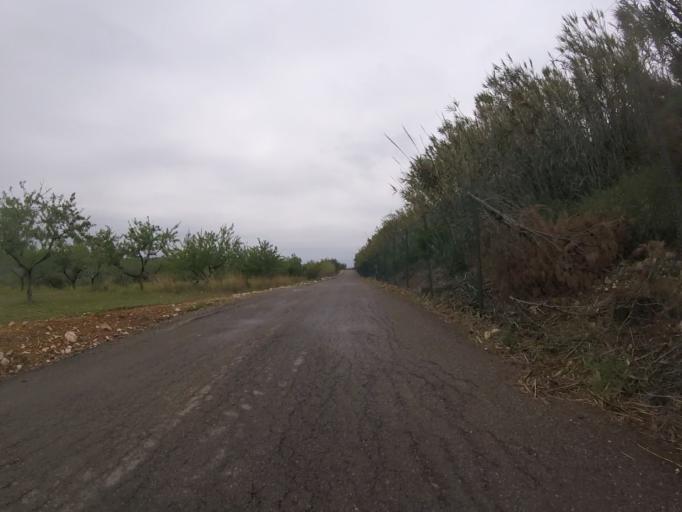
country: ES
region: Valencia
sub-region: Provincia de Castello
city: Alcala de Xivert
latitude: 40.2736
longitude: 0.2413
